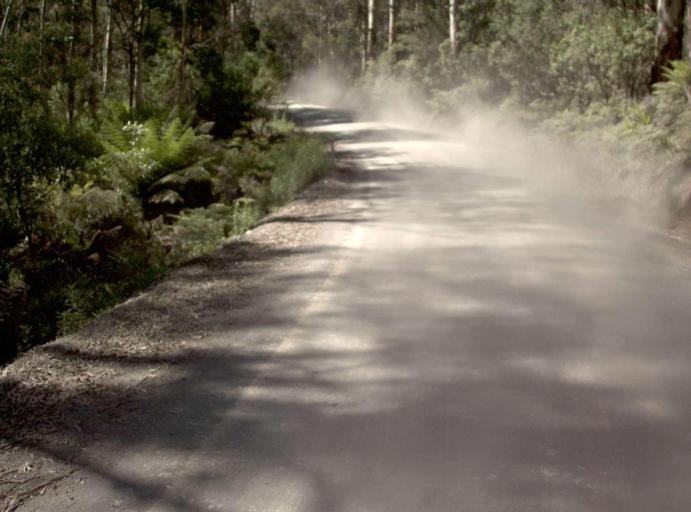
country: AU
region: New South Wales
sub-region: Bombala
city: Bombala
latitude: -37.2240
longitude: 148.7478
